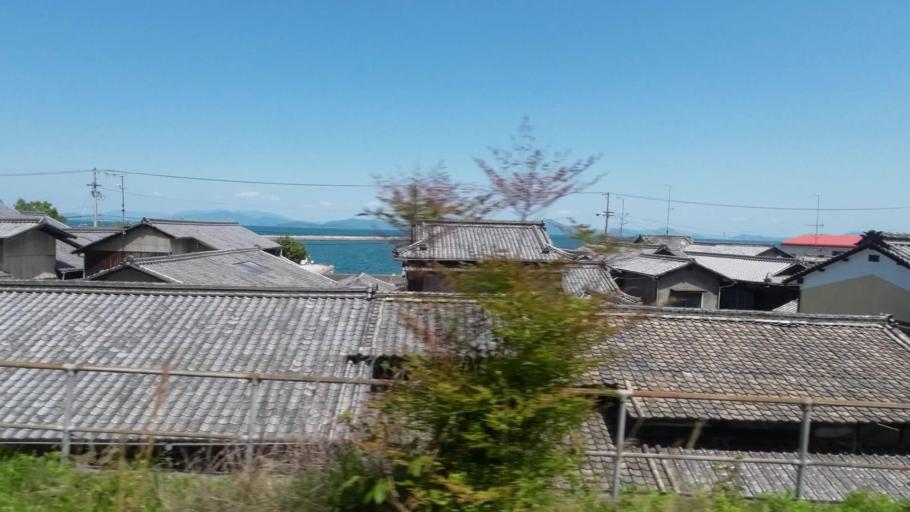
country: JP
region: Ehime
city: Hojo
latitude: 34.0318
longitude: 132.8332
